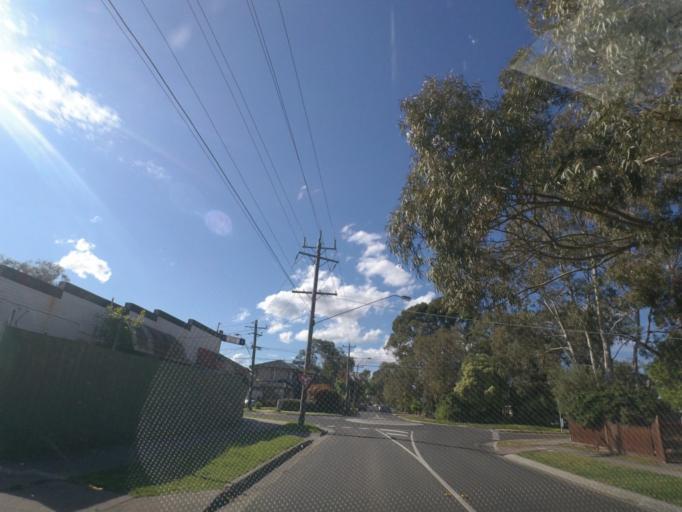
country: AU
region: Victoria
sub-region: Knox
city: Knoxfield
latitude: -37.8890
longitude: 145.2491
